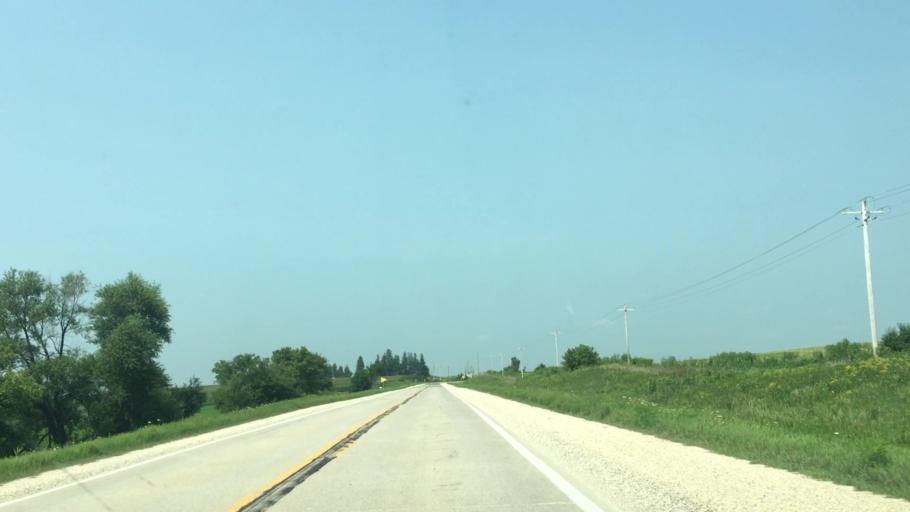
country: US
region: Iowa
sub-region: Fayette County
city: West Union
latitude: 43.1331
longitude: -91.8691
